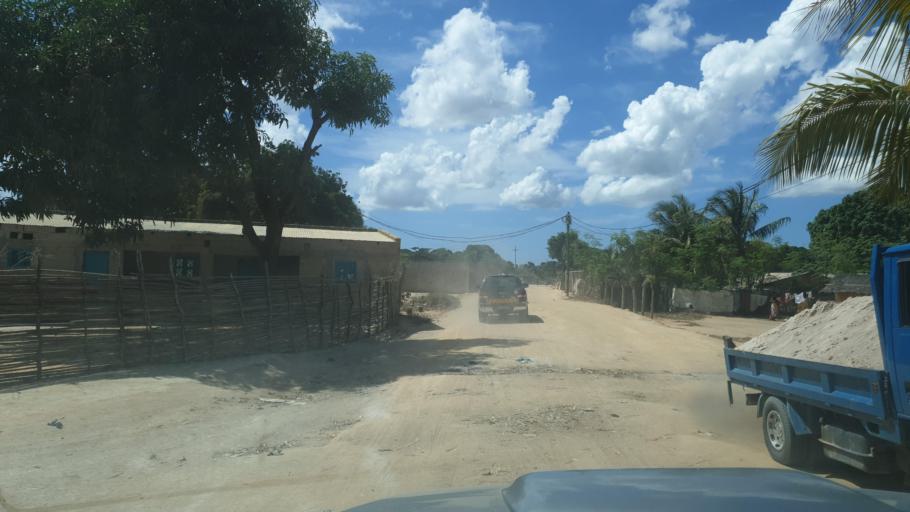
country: MZ
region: Nampula
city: Nacala
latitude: -14.5668
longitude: 40.6978
